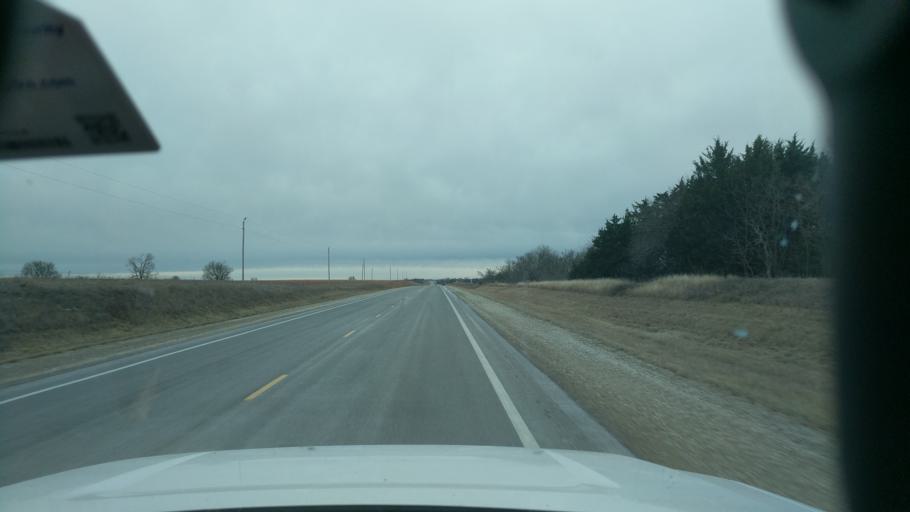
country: US
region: Kansas
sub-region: Marion County
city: Marion
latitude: 38.4593
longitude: -96.9577
